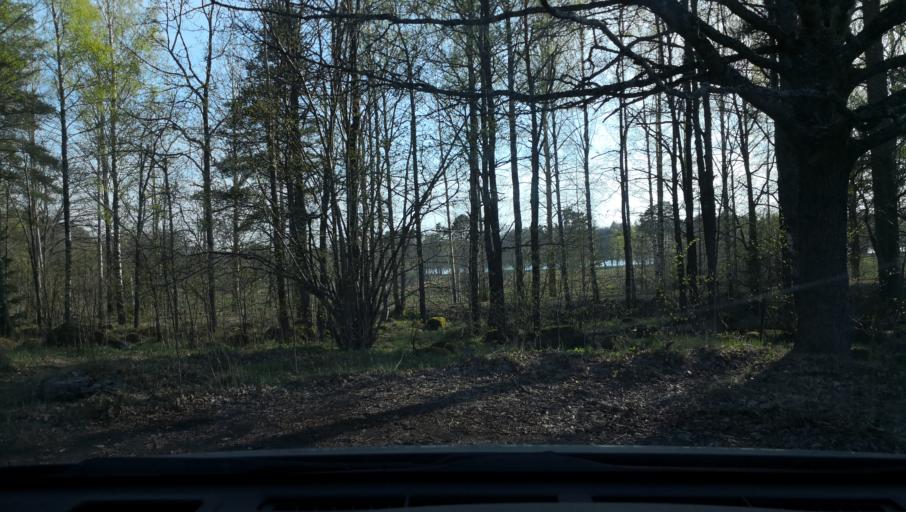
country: SE
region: Uppsala
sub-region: Heby Kommun
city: Tarnsjo
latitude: 60.2883
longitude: 16.8973
